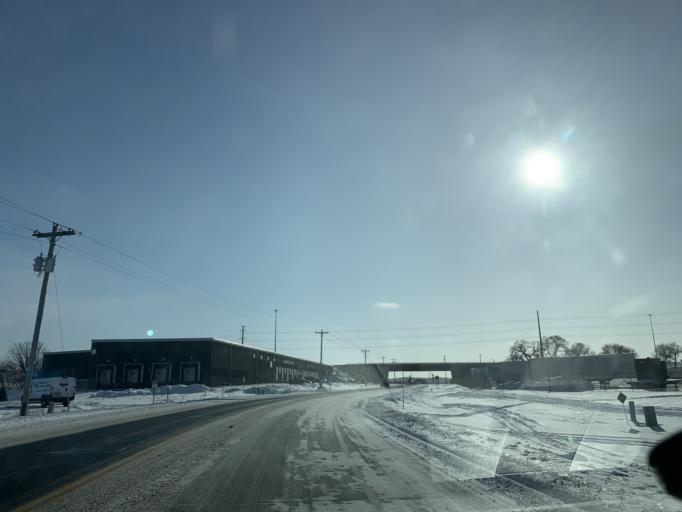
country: US
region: Minnesota
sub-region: Scott County
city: Savage
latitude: 44.7900
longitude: -93.4106
